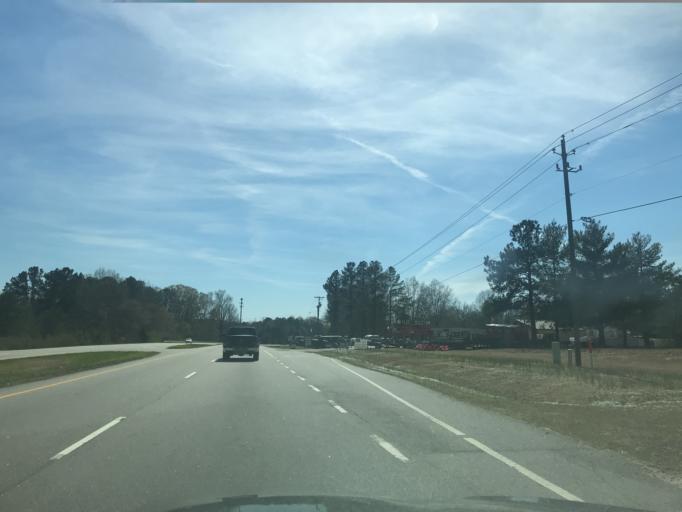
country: US
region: North Carolina
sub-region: Wake County
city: Garner
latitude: 35.6743
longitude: -78.6900
